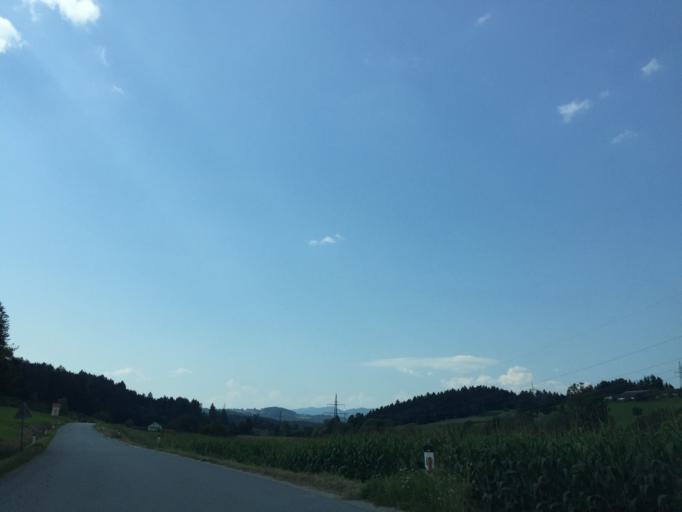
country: SI
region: Slovenj Gradec
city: Smartno pri Slovenj Gradcu
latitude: 46.4616
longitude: 15.0969
